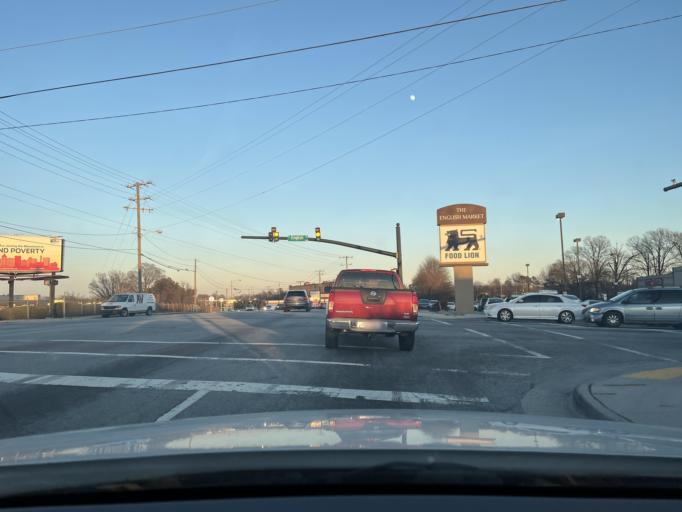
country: US
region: North Carolina
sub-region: Guilford County
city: Greensboro
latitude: 36.0763
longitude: -79.7579
